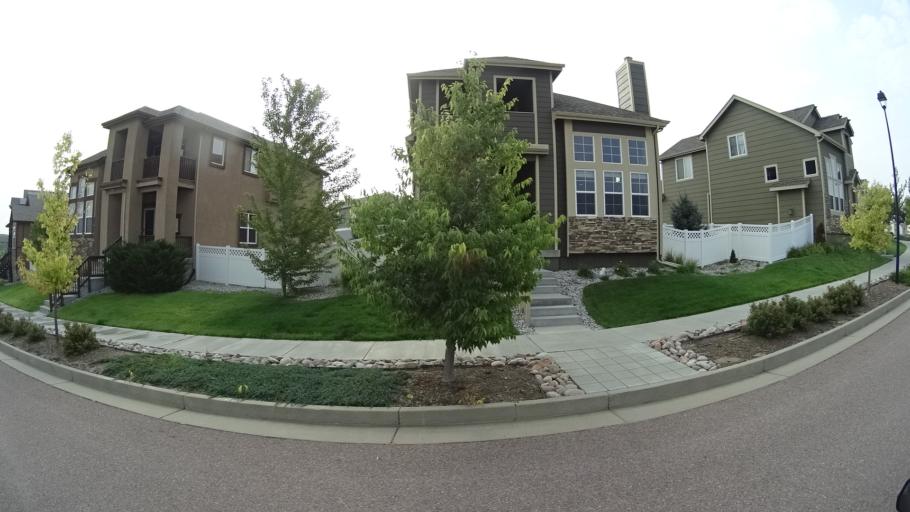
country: US
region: Colorado
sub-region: El Paso County
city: Stratmoor
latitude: 38.8116
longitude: -104.7874
